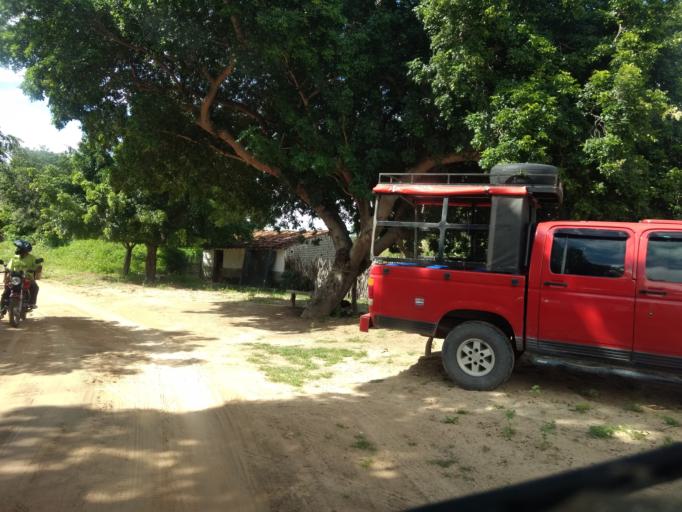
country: BR
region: Ceara
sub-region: Crateus
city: Crateus
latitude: -5.2004
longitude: -40.9551
